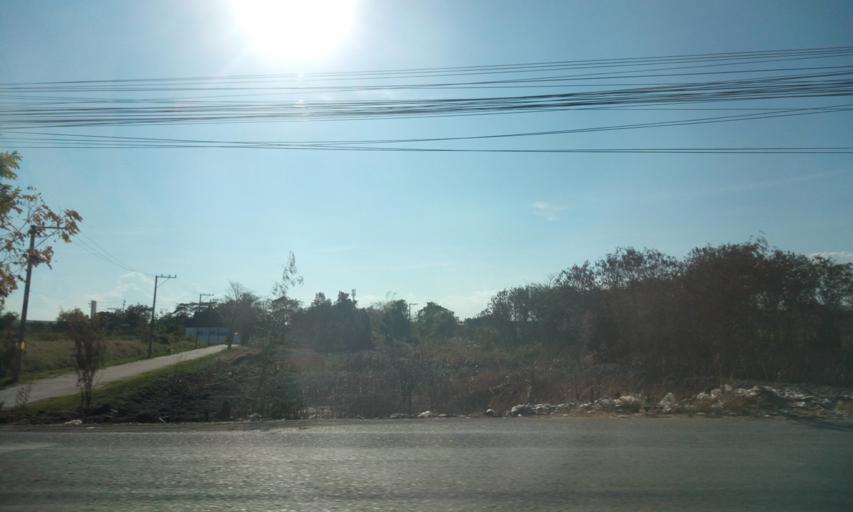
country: TH
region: Samut Prakan
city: Bang Bo District
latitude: 13.5888
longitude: 100.7600
